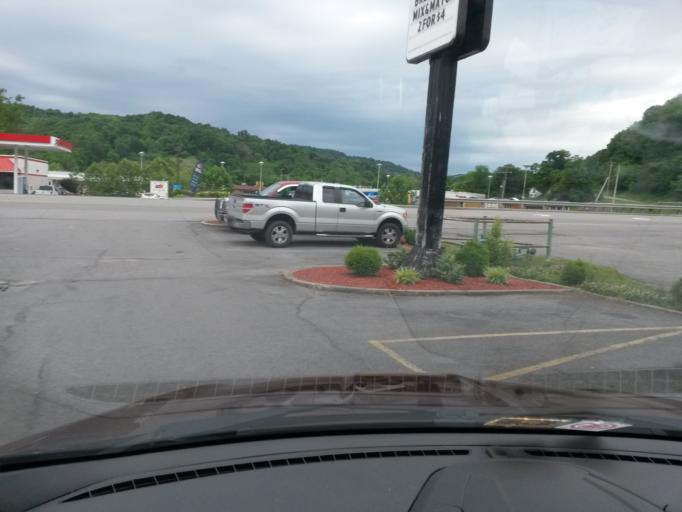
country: US
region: West Virginia
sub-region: Lewis County
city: Weston
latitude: 39.0362
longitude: -80.4493
